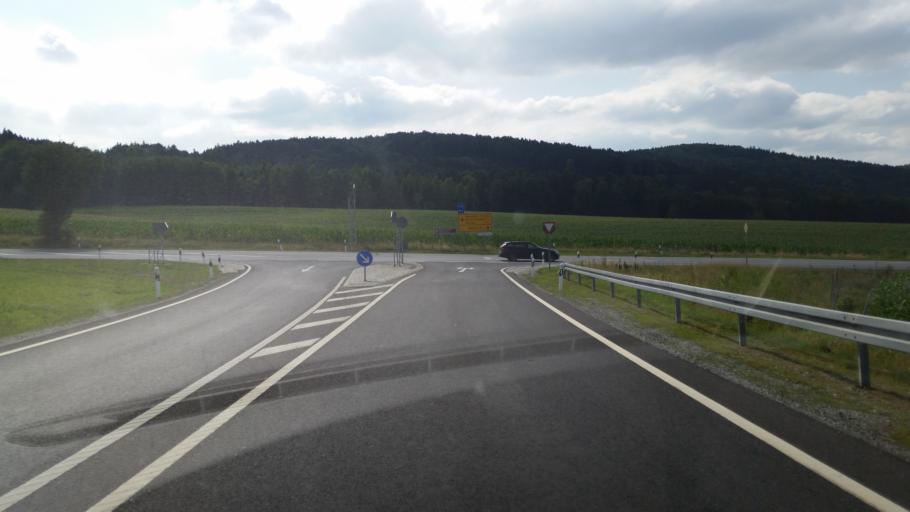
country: DE
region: Saxony
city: Rammenau
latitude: 51.1774
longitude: 14.1406
